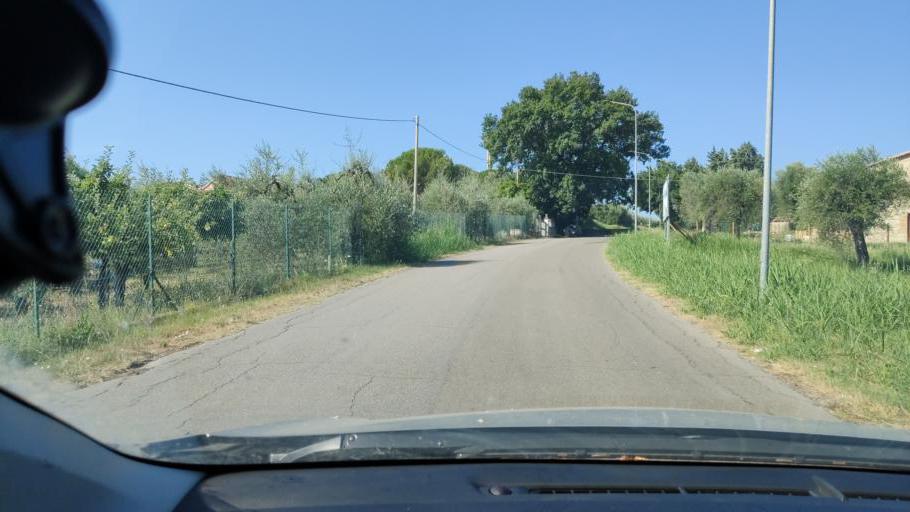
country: IT
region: Umbria
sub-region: Provincia di Terni
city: Fornole
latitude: 42.5162
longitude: 12.4307
